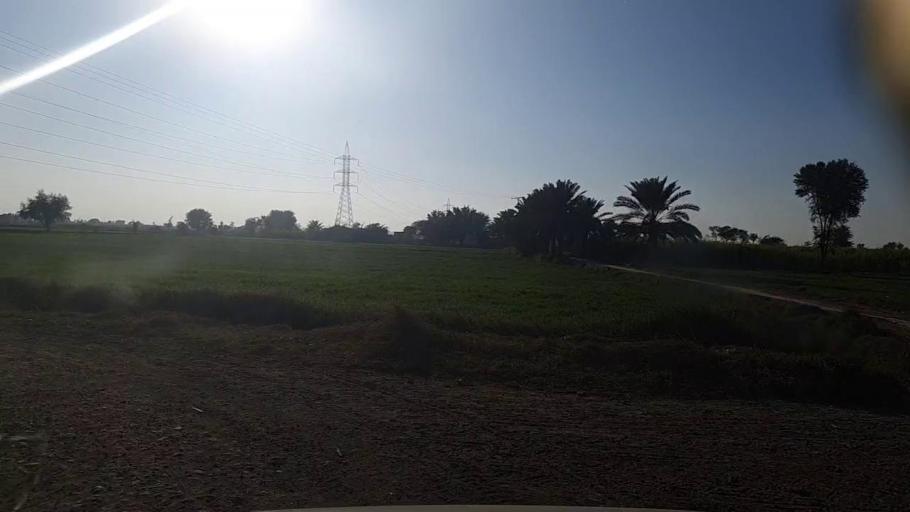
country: PK
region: Sindh
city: Khairpur
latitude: 28.0206
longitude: 69.7108
